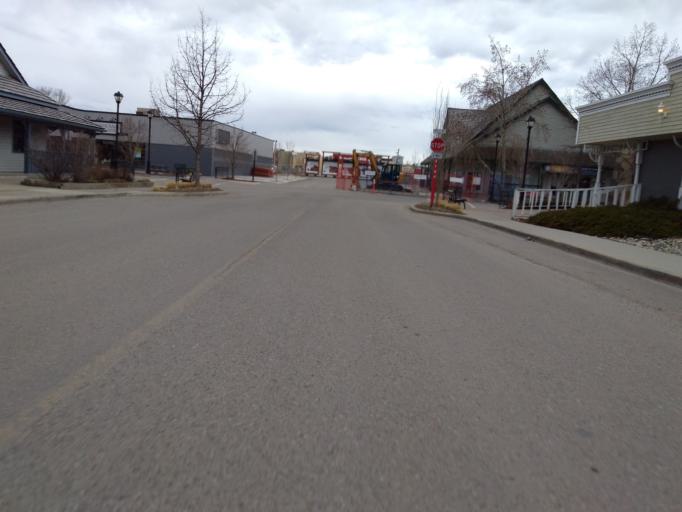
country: CA
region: Alberta
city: Cochrane
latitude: 51.1915
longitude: -114.4718
